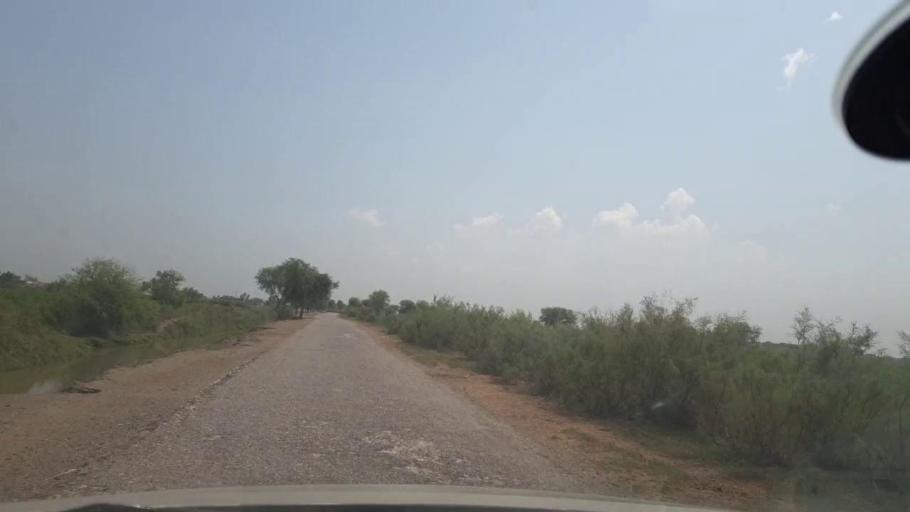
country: PK
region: Sindh
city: Jacobabad
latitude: 28.1311
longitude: 68.3799
